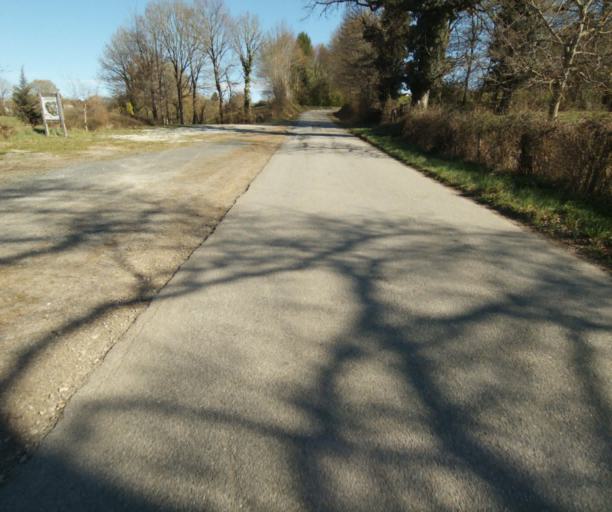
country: FR
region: Limousin
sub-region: Departement de la Correze
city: Chamboulive
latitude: 45.4680
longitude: 1.7295
